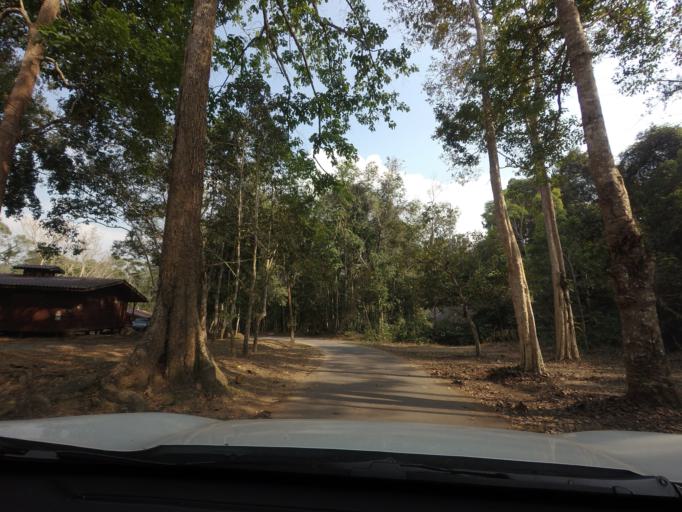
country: TH
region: Nakhon Ratchasima
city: Pak Chong
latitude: 14.4378
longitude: 101.3739
